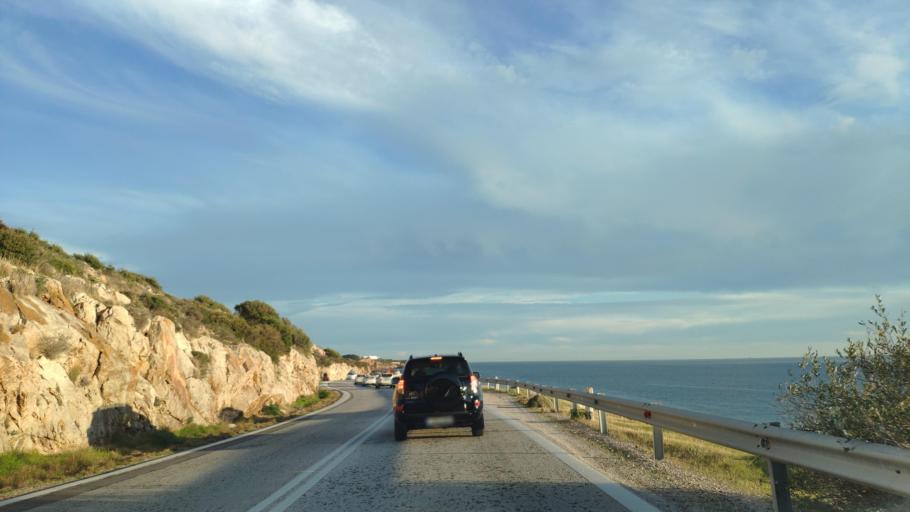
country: GR
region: Attica
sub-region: Nomarchia Anatolikis Attikis
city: Palaia Fokaia
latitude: 37.6668
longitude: 23.9614
